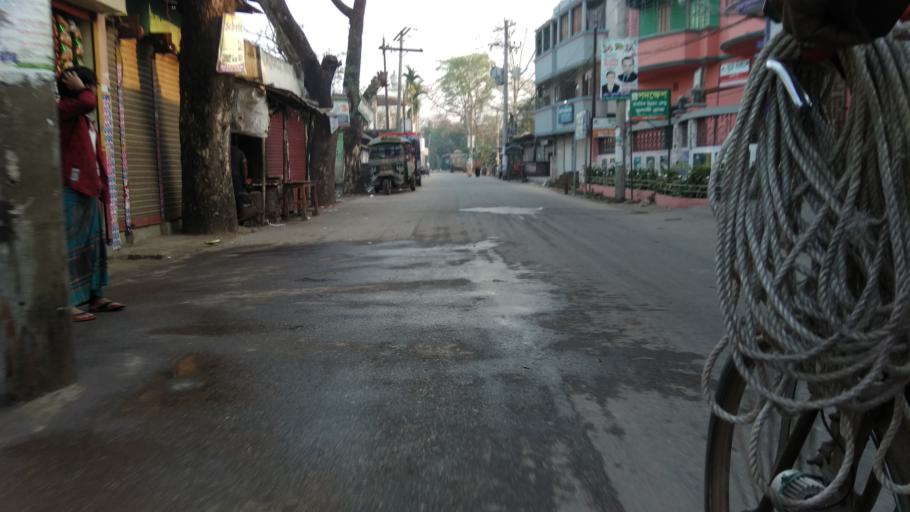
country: BD
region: Barisal
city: Mehendiganj
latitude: 22.9160
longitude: 90.4107
